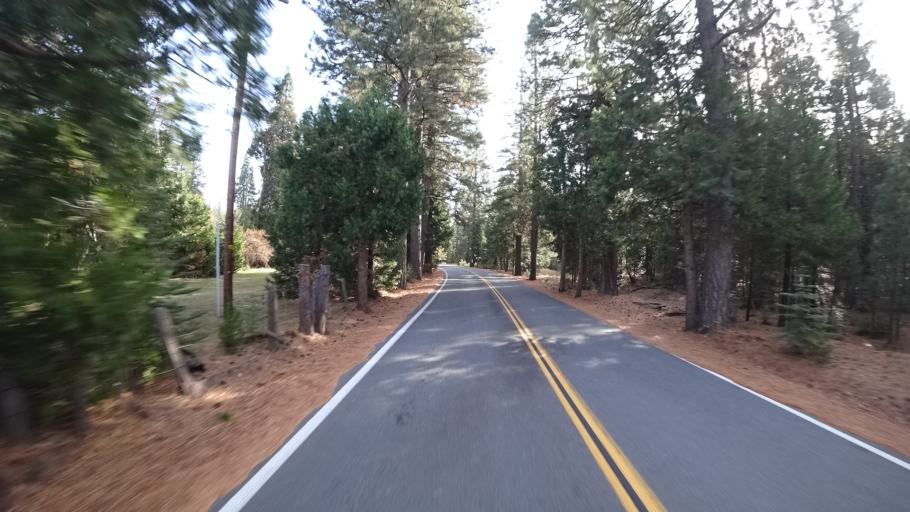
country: US
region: California
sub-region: Siskiyou County
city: Weed
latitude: 41.4047
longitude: -122.4284
